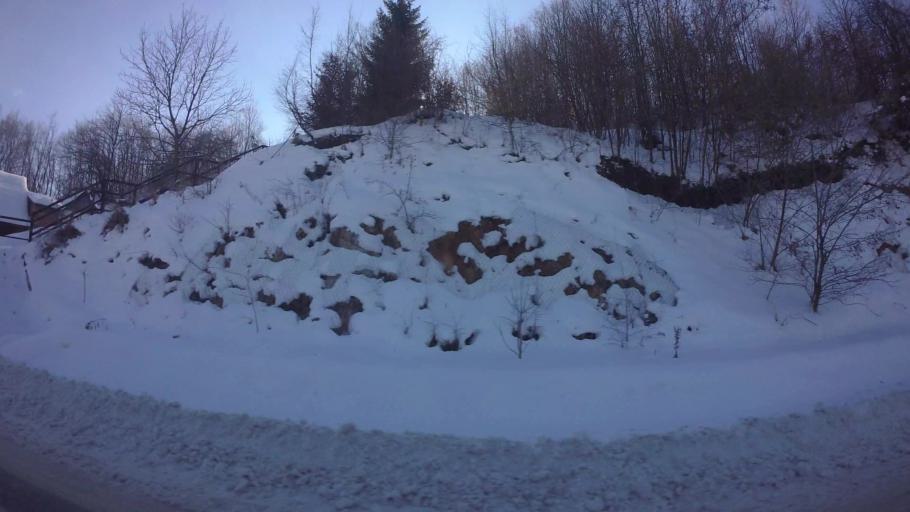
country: BA
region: Federation of Bosnia and Herzegovina
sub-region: Kanton Sarajevo
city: Sarajevo
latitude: 43.7915
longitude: 18.3541
